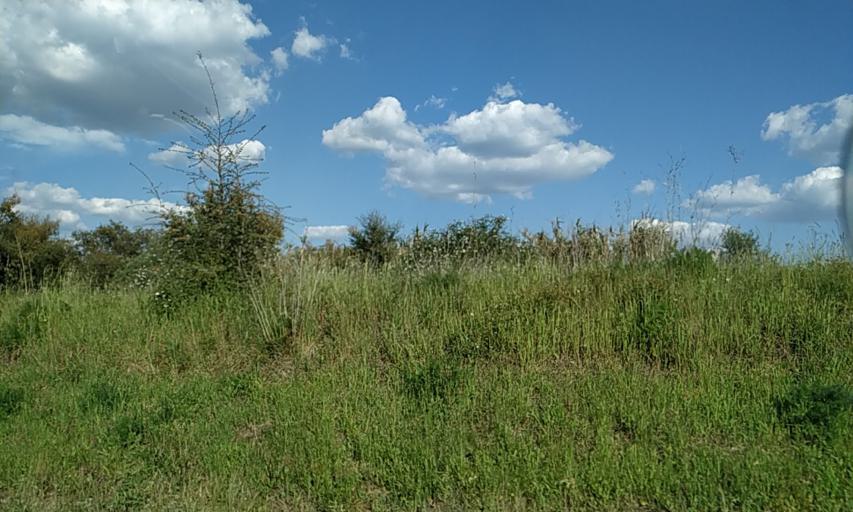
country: PT
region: Evora
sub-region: Estremoz
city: Estremoz
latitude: 38.8721
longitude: -7.5639
